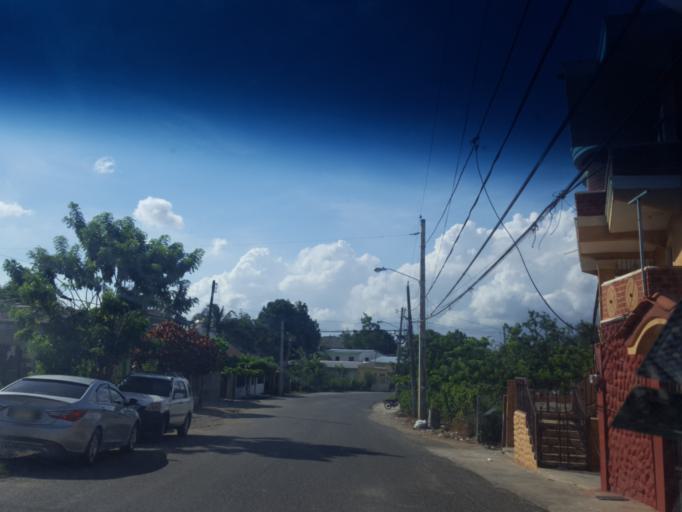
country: DO
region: La Vega
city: Rio Verde Arriba
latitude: 19.3594
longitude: -70.6053
